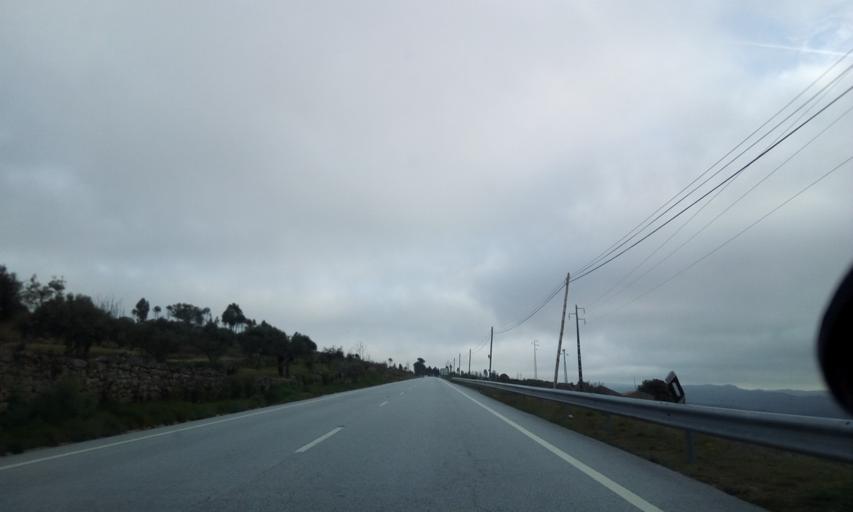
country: PT
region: Guarda
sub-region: Fornos de Algodres
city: Fornos de Algodres
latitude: 40.6607
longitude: -7.4785
